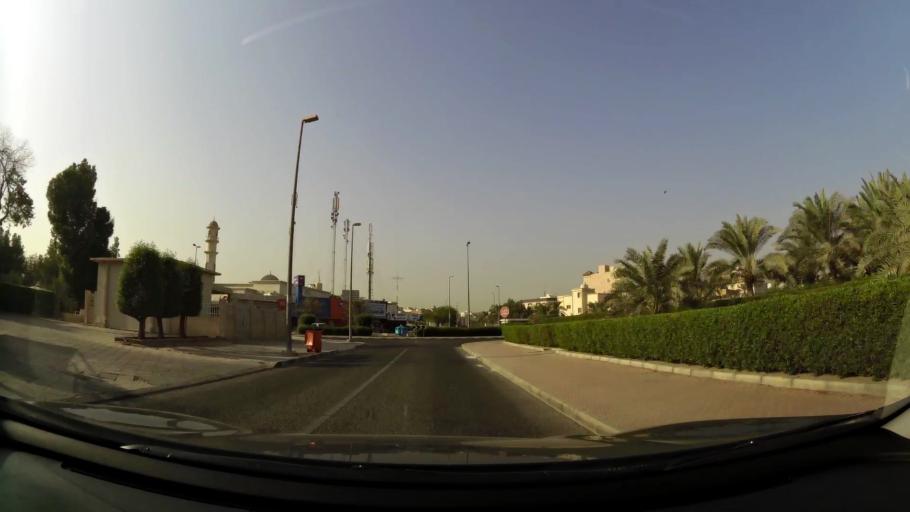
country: KW
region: Al Asimah
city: Ad Dasmah
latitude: 29.3627
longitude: 48.0068
